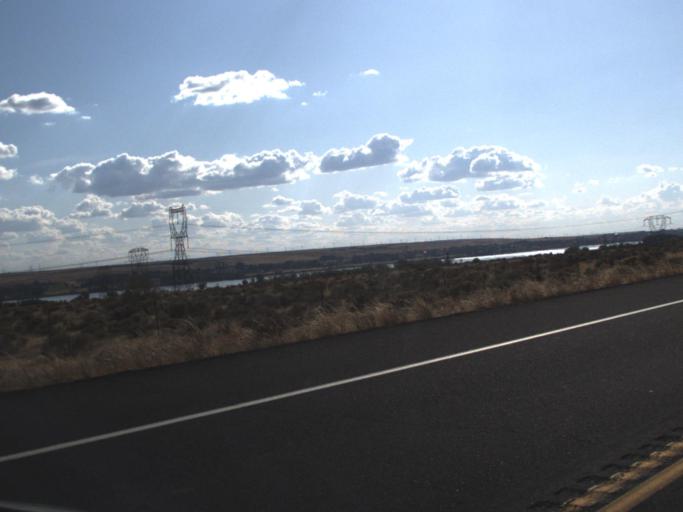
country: US
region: Oregon
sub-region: Umatilla County
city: Umatilla
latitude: 45.9440
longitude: -119.3417
